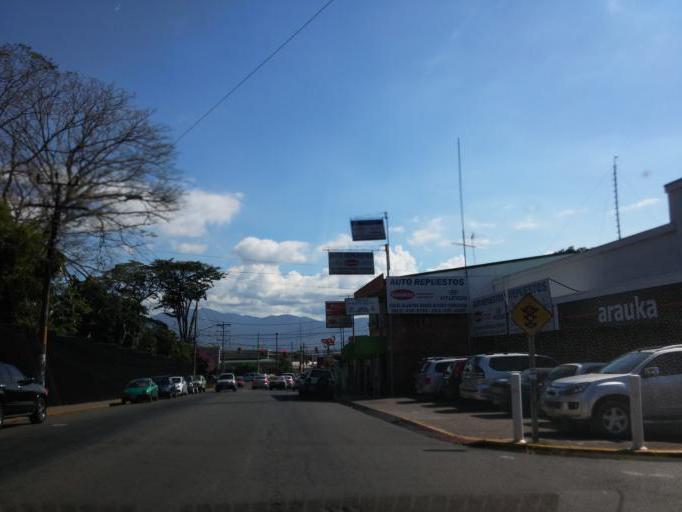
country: CR
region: Alajuela
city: Alajuela
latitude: 10.0141
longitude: -84.2082
